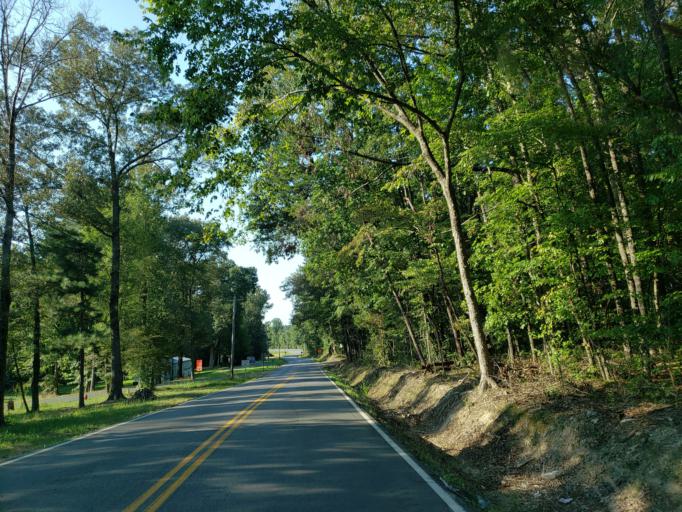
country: US
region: Tennessee
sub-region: Bradley County
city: Wildwood Lake
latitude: 35.0426
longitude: -84.7450
